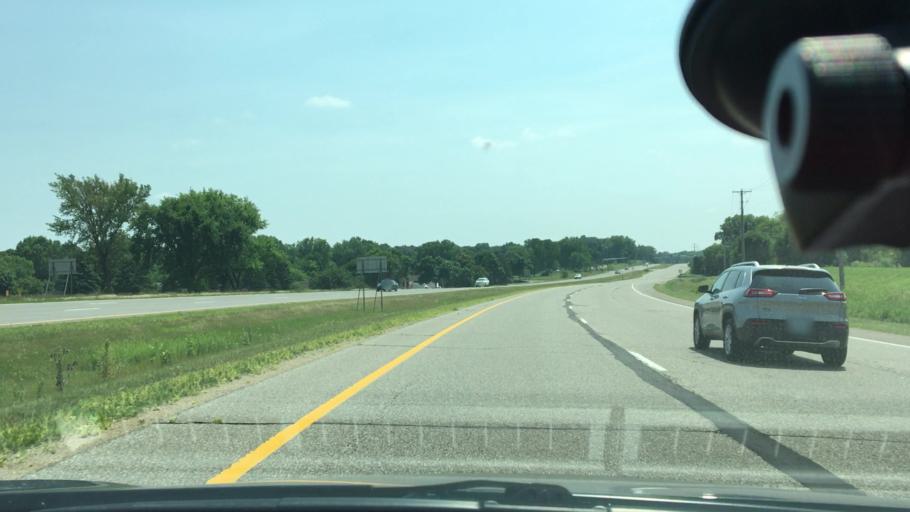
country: US
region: Minnesota
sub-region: Hennepin County
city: Plymouth
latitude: 45.0063
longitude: -93.4474
